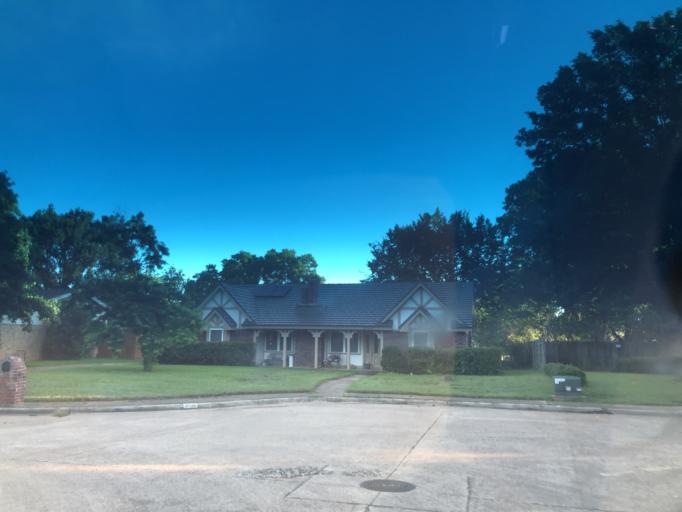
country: US
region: Texas
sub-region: Dallas County
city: Grand Prairie
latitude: 32.7827
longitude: -97.0347
